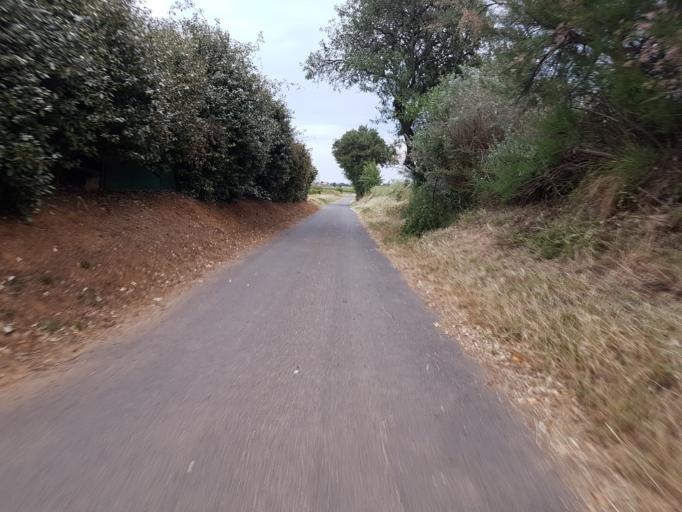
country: FR
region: Languedoc-Roussillon
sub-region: Departement de l'Herault
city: Cers
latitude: 43.3214
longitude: 3.3157
